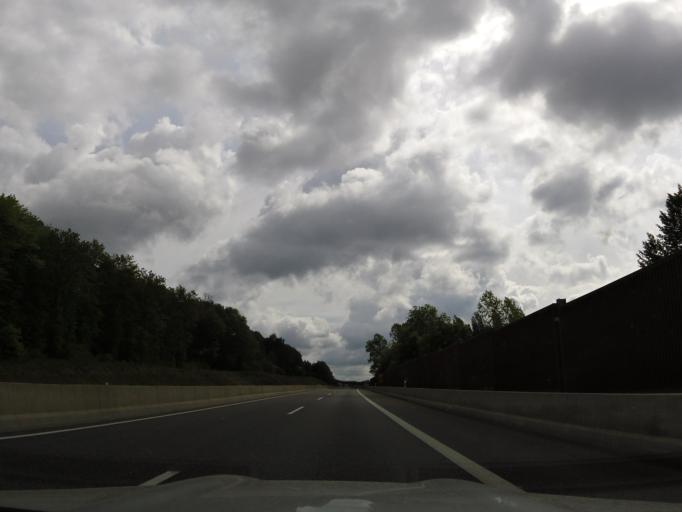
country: DE
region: Hesse
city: Merenberg
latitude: 50.5000
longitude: 8.2033
